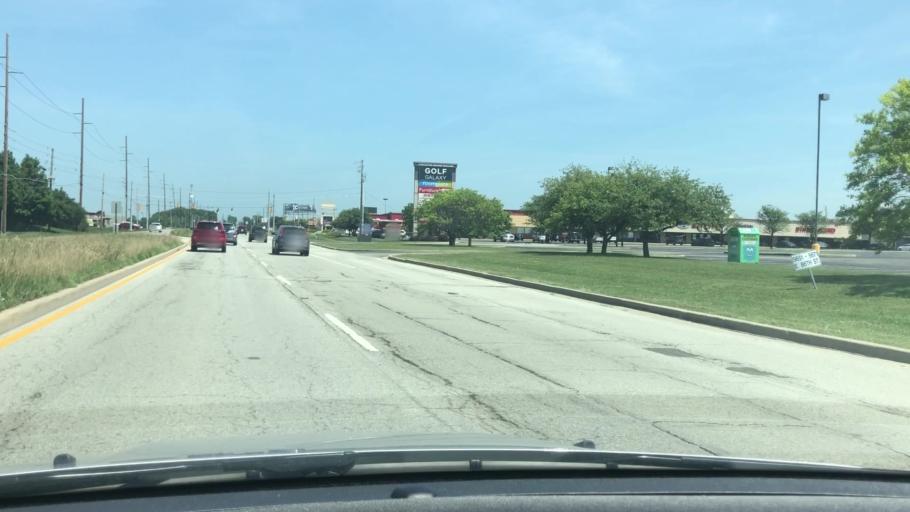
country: US
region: Indiana
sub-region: Hamilton County
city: Fishers
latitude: 39.9124
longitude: -86.0715
